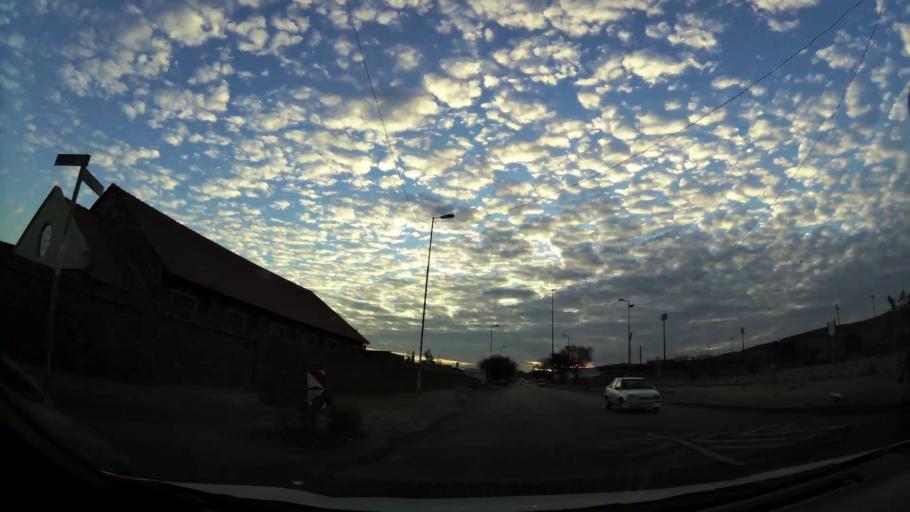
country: ZA
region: Gauteng
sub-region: City of Tshwane Metropolitan Municipality
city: Pretoria
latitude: -25.7110
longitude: 28.3421
